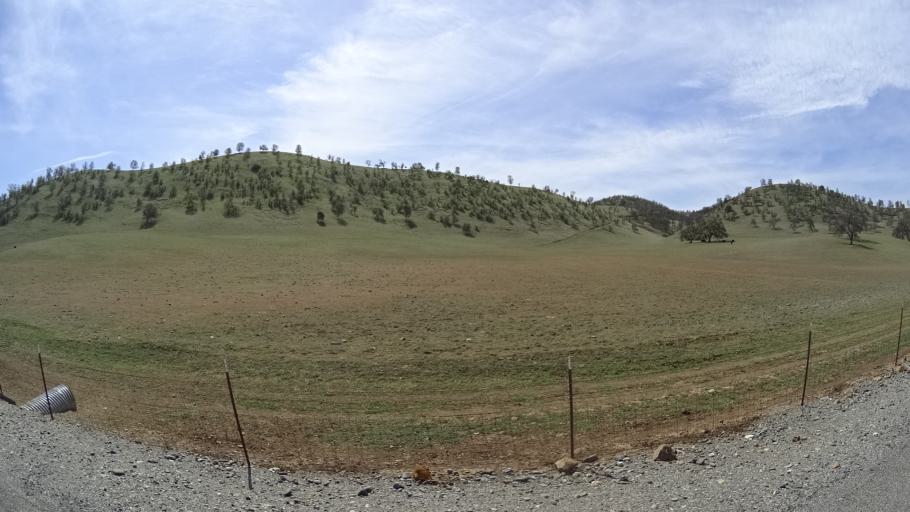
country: US
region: California
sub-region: Glenn County
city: Willows
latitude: 39.5393
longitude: -122.4450
